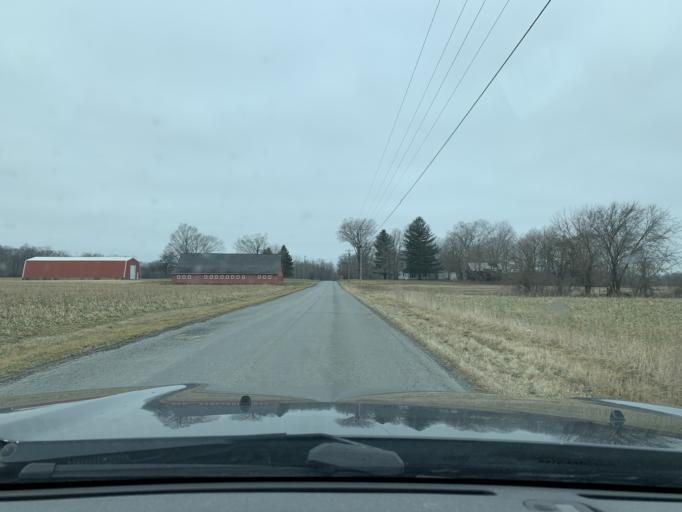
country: US
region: Indiana
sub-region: Porter County
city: Chesterton
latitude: 41.6070
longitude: -86.9926
